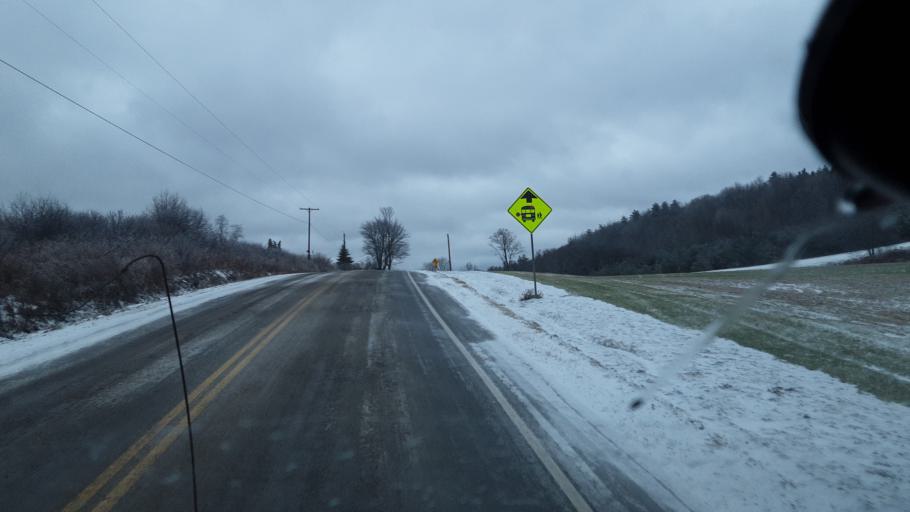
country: US
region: New York
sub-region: Allegany County
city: Friendship
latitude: 42.2419
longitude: -78.1437
